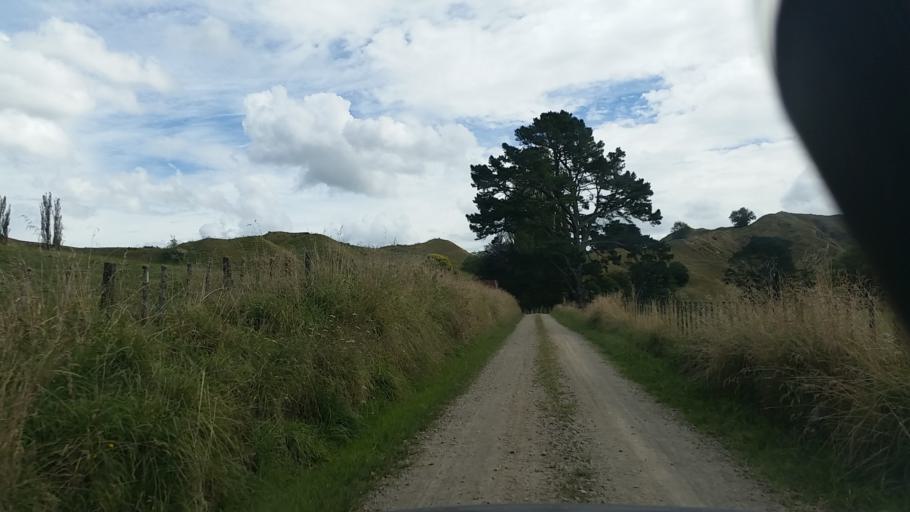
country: NZ
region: Taranaki
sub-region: South Taranaki District
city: Eltham
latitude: -39.2588
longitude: 174.5581
